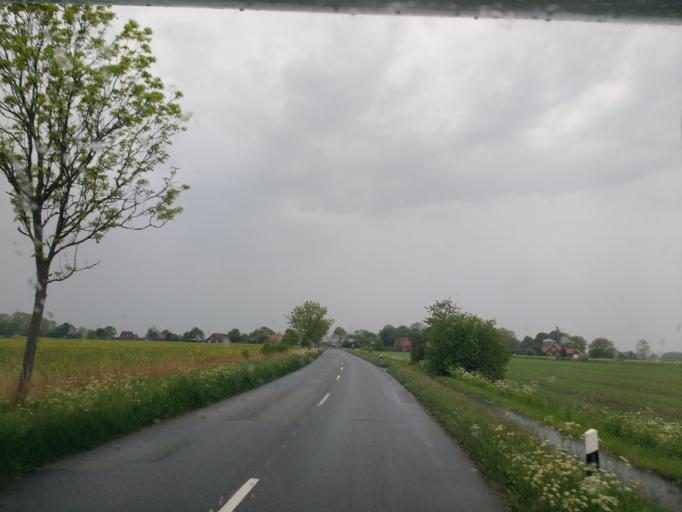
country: DE
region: Lower Saxony
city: Schillig
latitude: 53.6971
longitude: 8.0027
